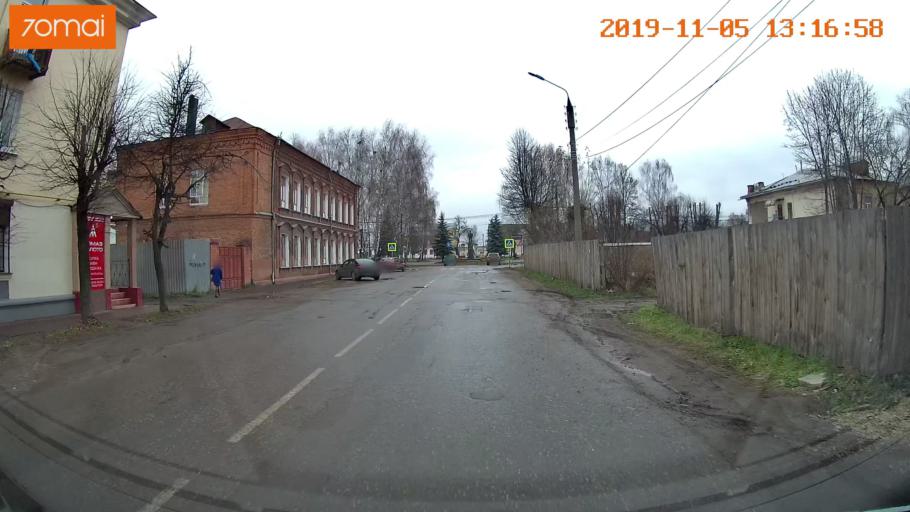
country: RU
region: Ivanovo
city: Shuya
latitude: 56.8538
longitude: 41.3775
